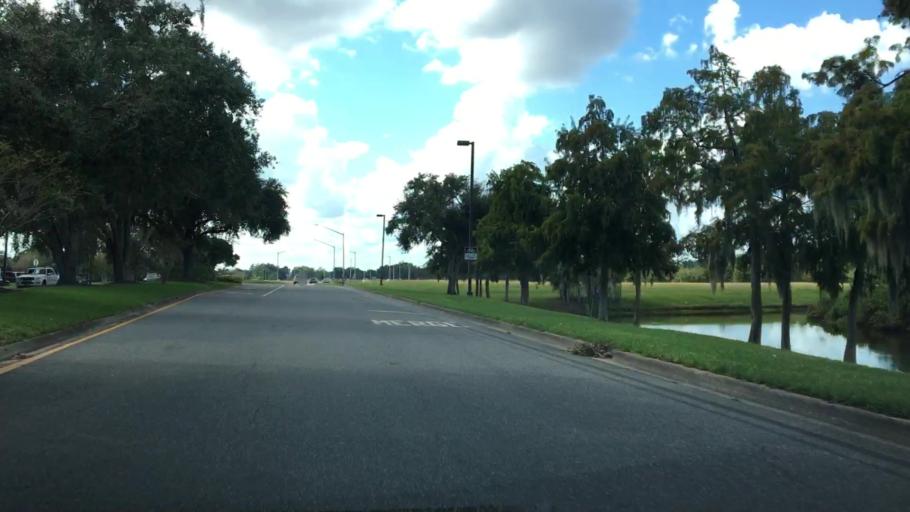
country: US
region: Florida
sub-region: Orange County
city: Conway
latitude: 28.4685
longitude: -81.3154
